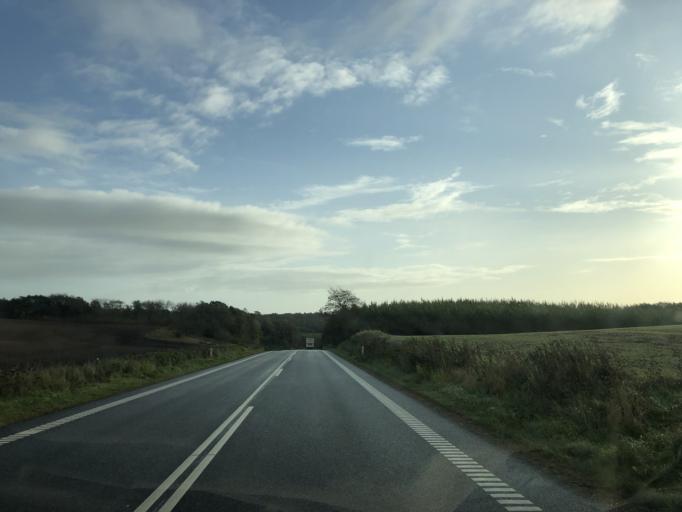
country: DK
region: North Denmark
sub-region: Mariagerfjord Kommune
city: Hobro
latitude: 56.6152
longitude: 9.6620
